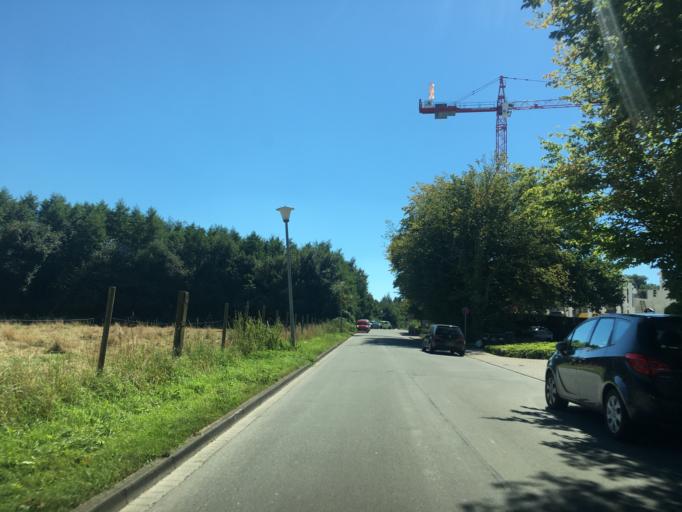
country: DE
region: North Rhine-Westphalia
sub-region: Regierungsbezirk Munster
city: Muenster
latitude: 51.9840
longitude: 7.6214
